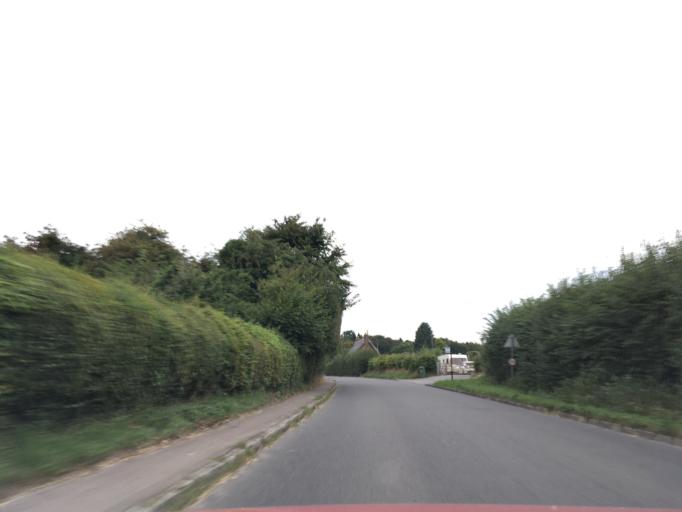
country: GB
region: England
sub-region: Wiltshire
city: Bremhill
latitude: 51.4098
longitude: -2.0508
